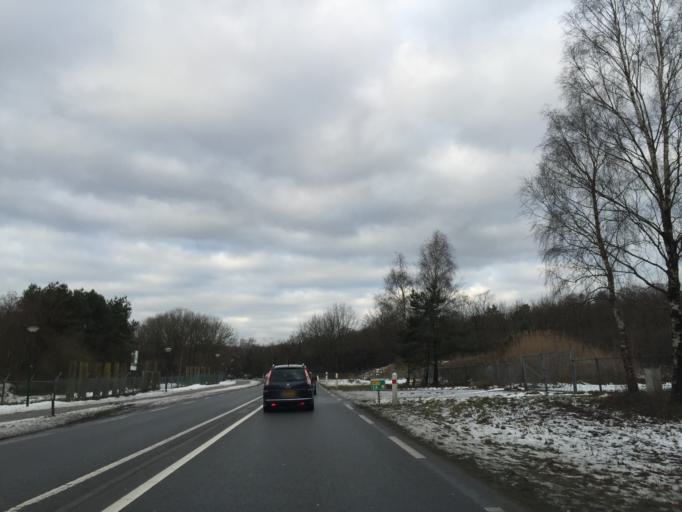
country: NL
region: Utrecht
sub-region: Gemeente Soest
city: Soest
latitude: 52.1301
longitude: 5.2980
